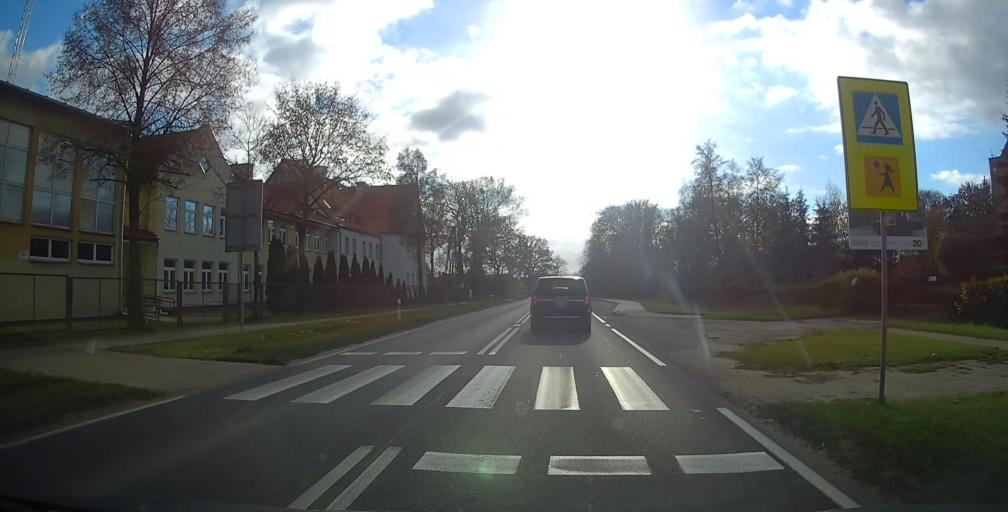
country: PL
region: Warmian-Masurian Voivodeship
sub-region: Powiat elcki
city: Elk
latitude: 53.7702
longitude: 22.3360
